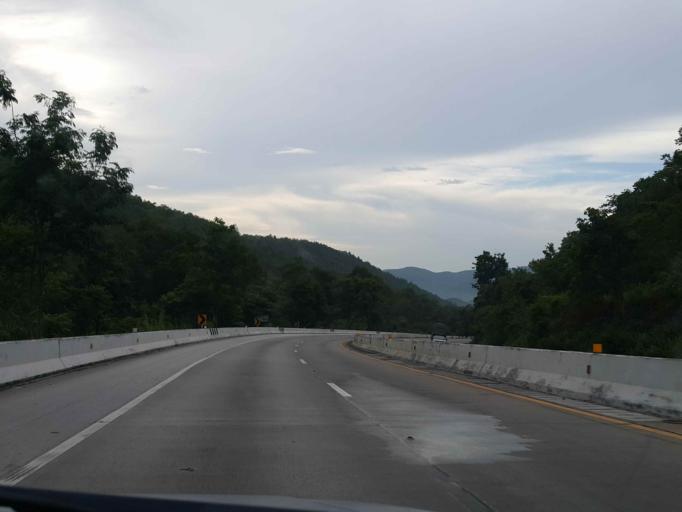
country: TH
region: Lamphun
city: Mae Tha
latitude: 18.4332
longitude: 99.2063
